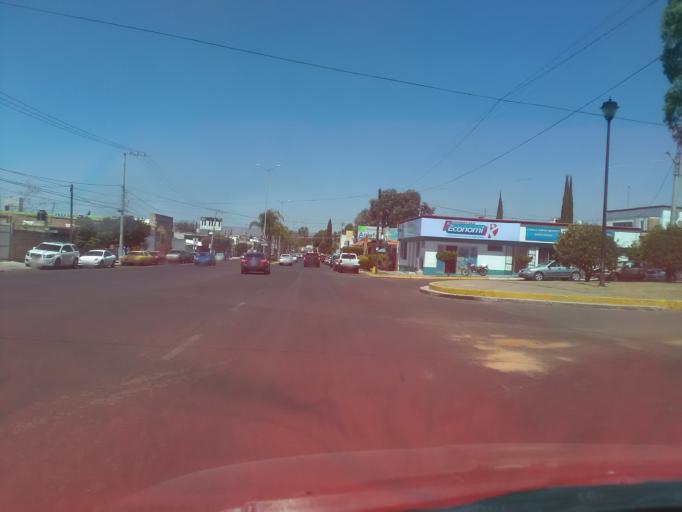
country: MX
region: Durango
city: Victoria de Durango
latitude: 24.0141
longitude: -104.6776
